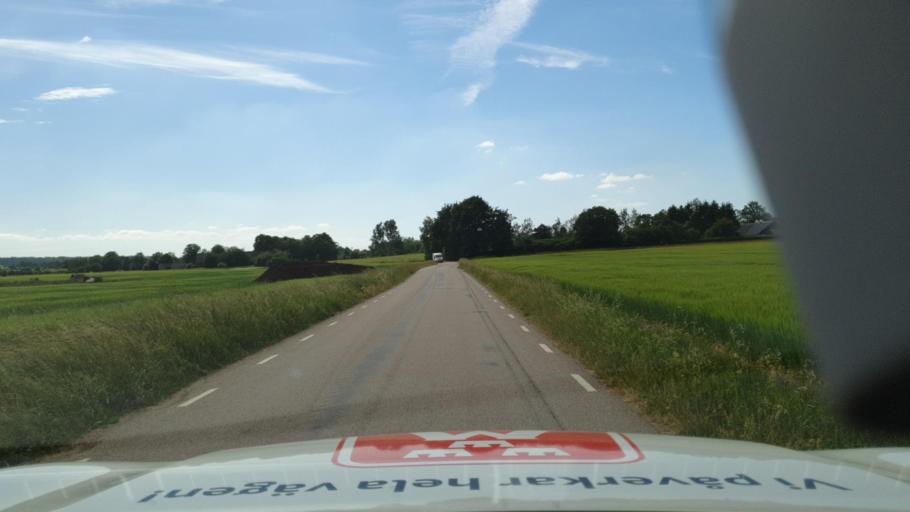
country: SE
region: Skane
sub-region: Sjobo Kommun
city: Sjoebo
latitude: 55.6383
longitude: 13.7902
